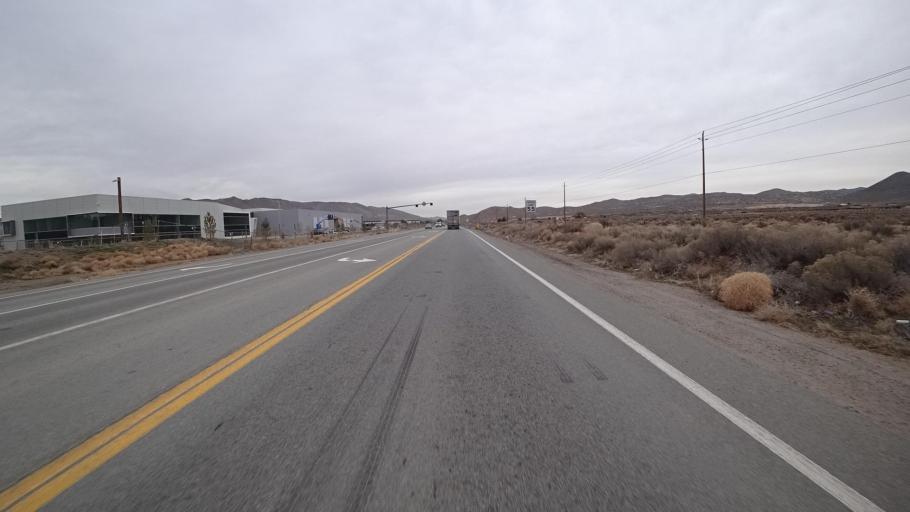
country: US
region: Nevada
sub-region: Washoe County
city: Spanish Springs
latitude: 39.6667
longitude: -119.7029
